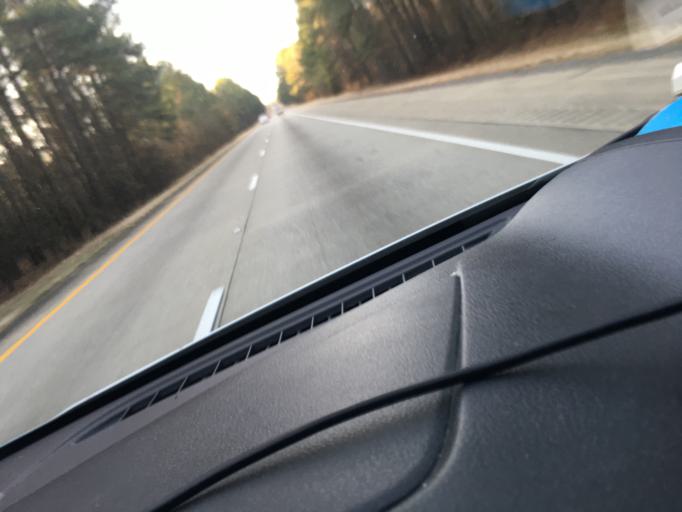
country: US
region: Arkansas
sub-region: Hot Spring County
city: Malvern
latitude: 34.4427
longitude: -92.7747
